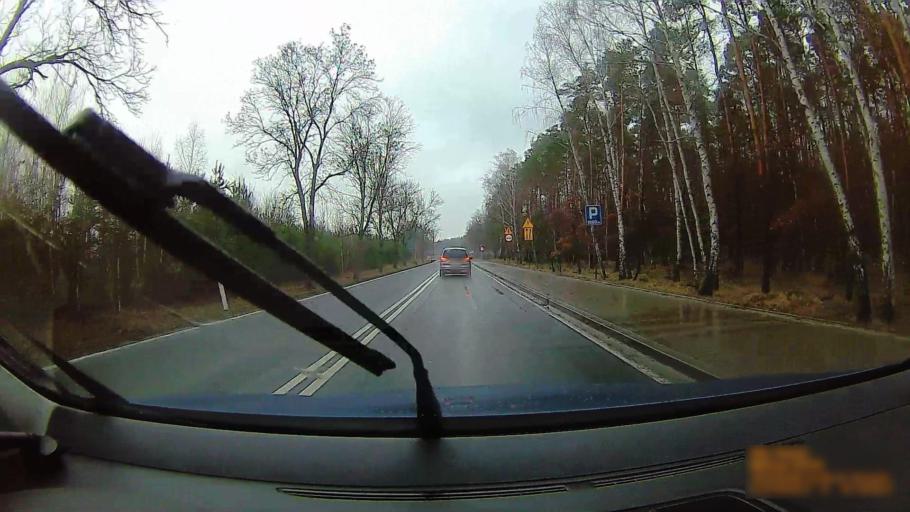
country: PL
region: Greater Poland Voivodeship
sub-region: Powiat koninski
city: Stare Miasto
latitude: 52.1583
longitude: 18.2740
